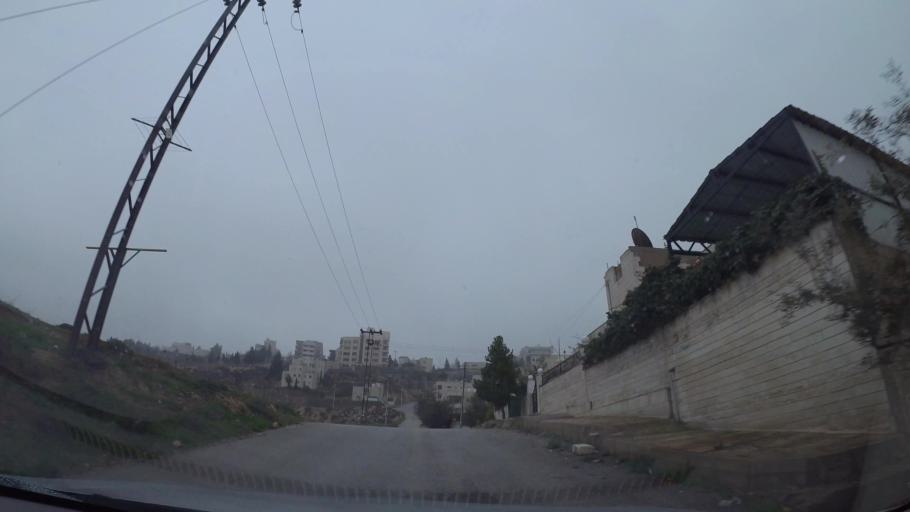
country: JO
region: Amman
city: Al Jubayhah
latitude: 32.0366
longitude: 35.8537
